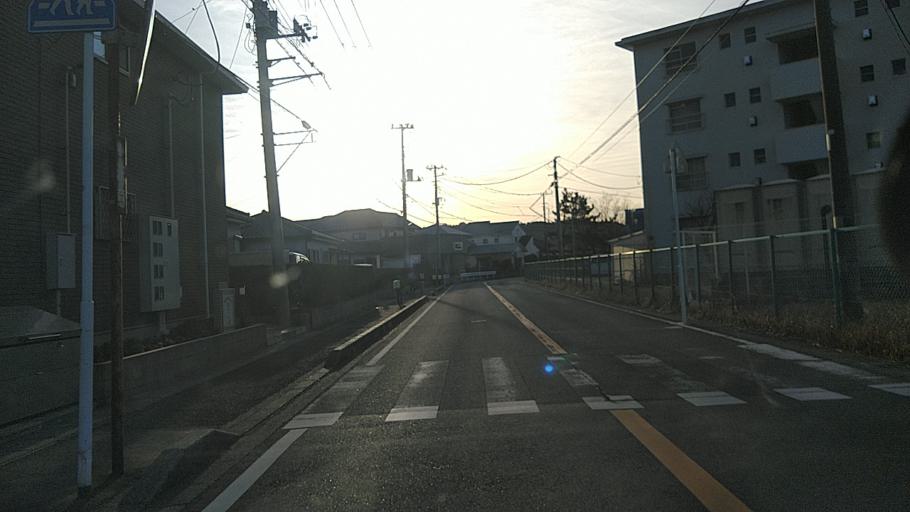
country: JP
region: Chiba
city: Kimitsu
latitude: 35.3061
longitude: 139.9242
